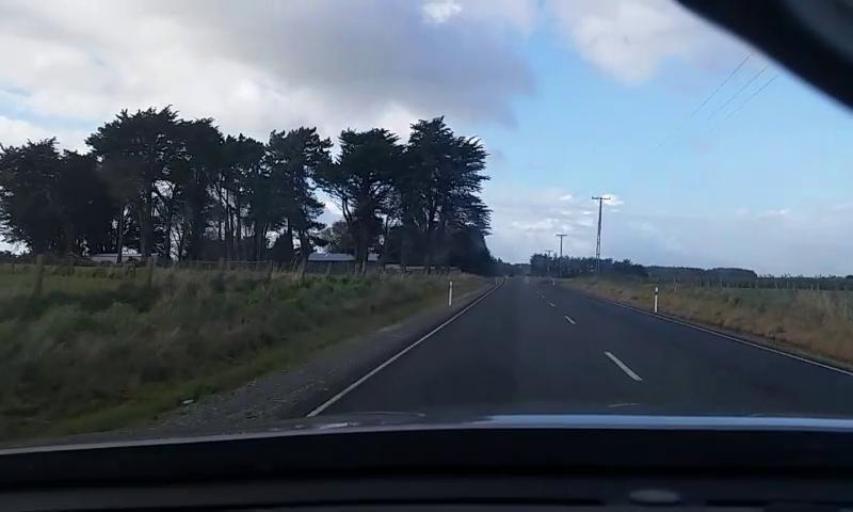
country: NZ
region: Southland
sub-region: Invercargill City
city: Invercargill
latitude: -46.3807
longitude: 168.4201
